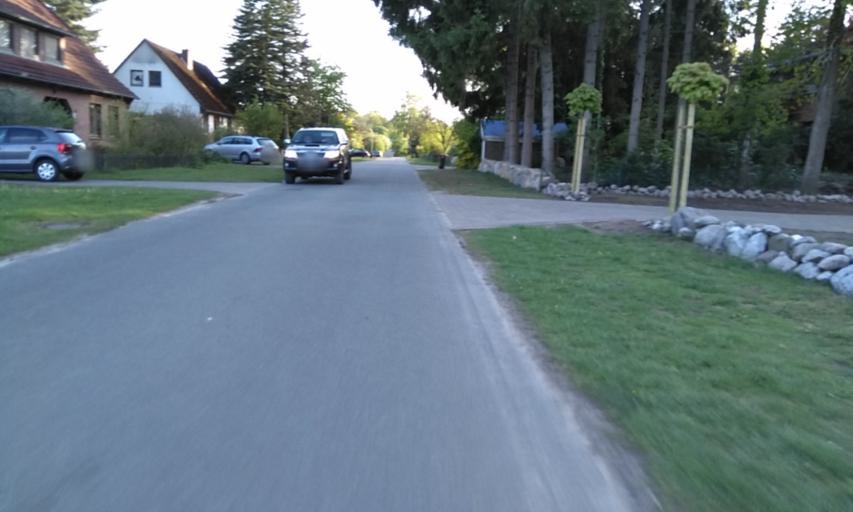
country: DE
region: Lower Saxony
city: Wohnste
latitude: 53.3870
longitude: 9.5555
